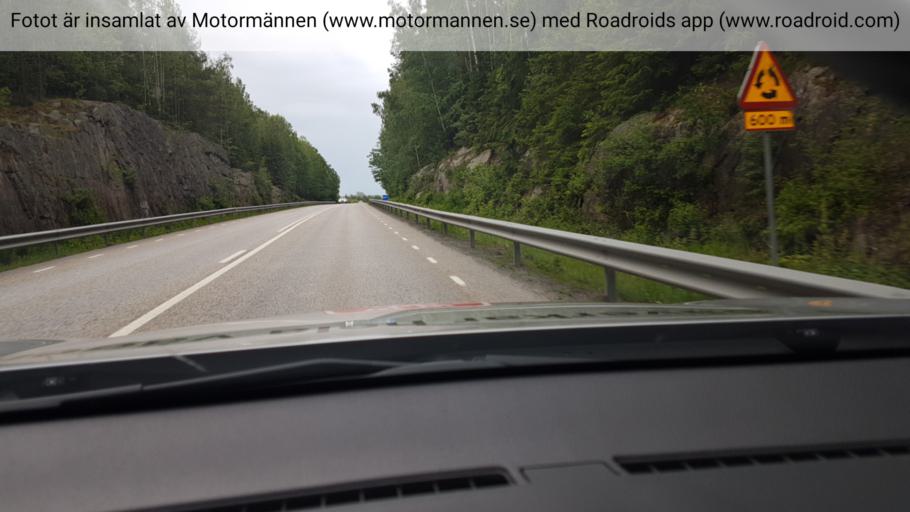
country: SE
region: Joenkoeping
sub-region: Habo Kommun
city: Habo
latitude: 57.9049
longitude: 14.1051
